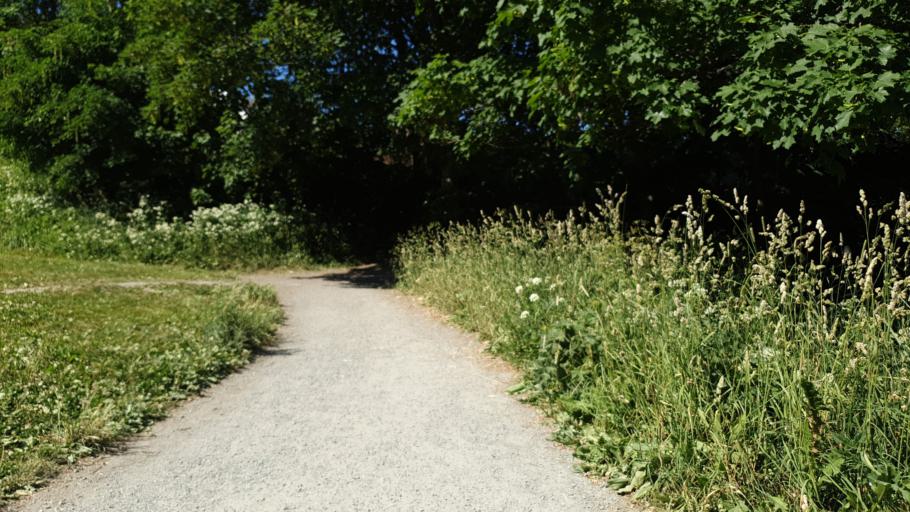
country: NO
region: Sor-Trondelag
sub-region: Trondheim
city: Trondheim
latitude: 63.4483
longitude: 10.4658
